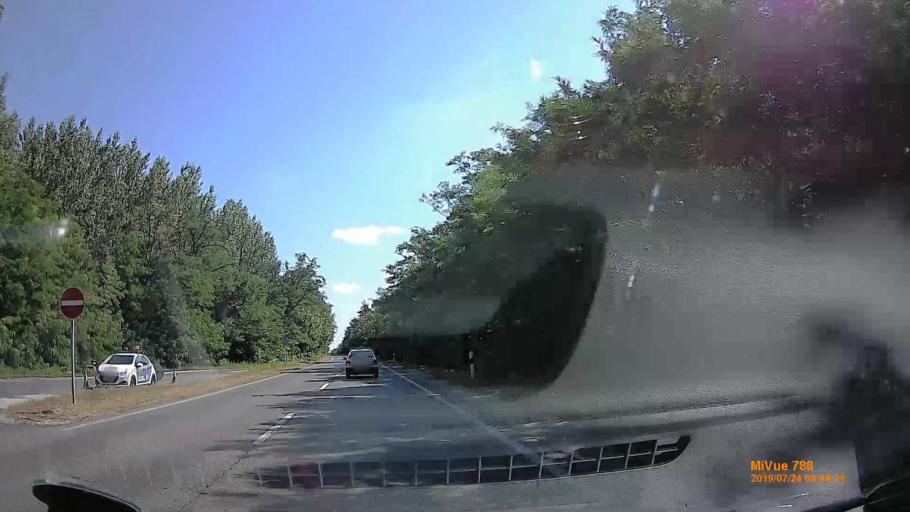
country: HU
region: Szabolcs-Szatmar-Bereg
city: Baktaloranthaza
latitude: 48.0027
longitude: 22.1142
